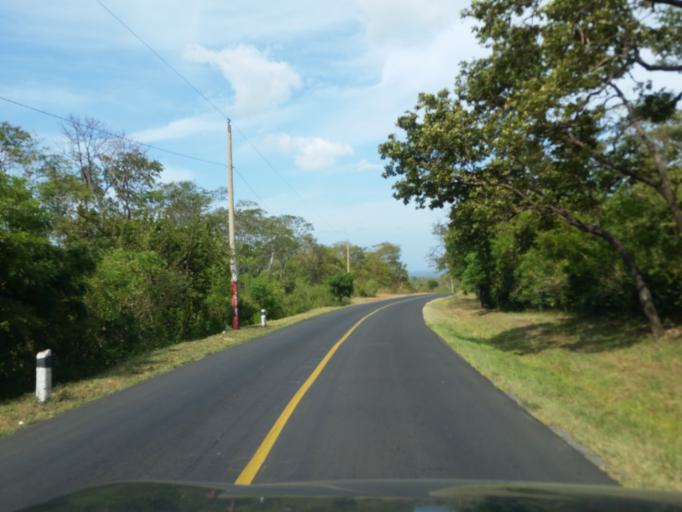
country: NI
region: Managua
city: San Rafael del Sur
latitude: 11.9144
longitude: -86.3698
